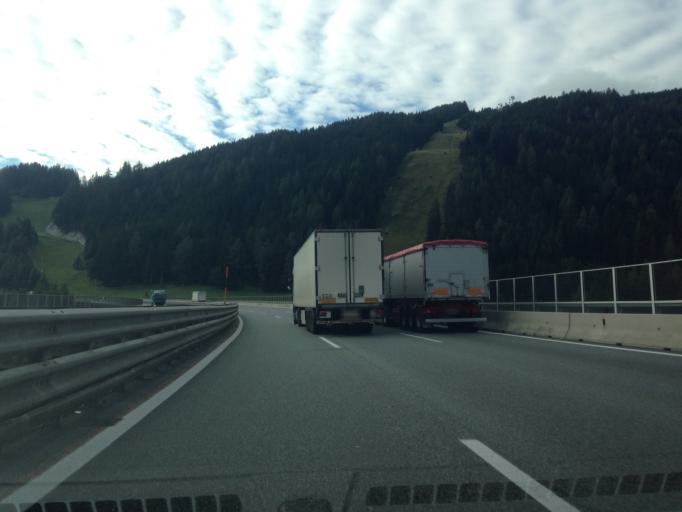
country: AT
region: Tyrol
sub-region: Politischer Bezirk Innsbruck Land
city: Steinach am Brenner
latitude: 47.0880
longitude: 11.4585
